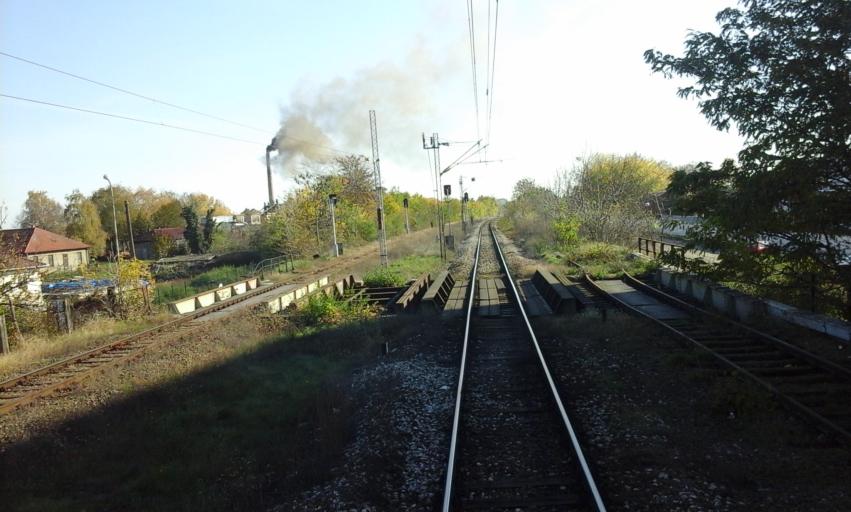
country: RS
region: Autonomna Pokrajina Vojvodina
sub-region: Severnobacki Okrug
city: Subotica
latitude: 46.0915
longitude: 19.6831
